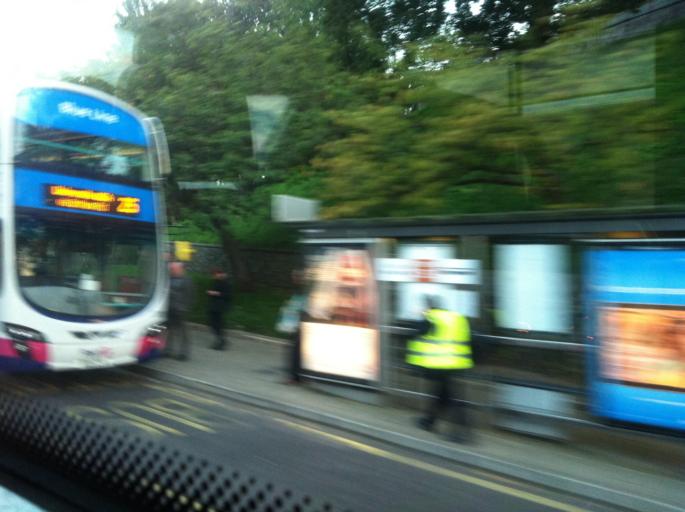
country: GB
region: England
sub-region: Norfolk
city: Norwich
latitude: 52.6293
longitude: 1.2960
